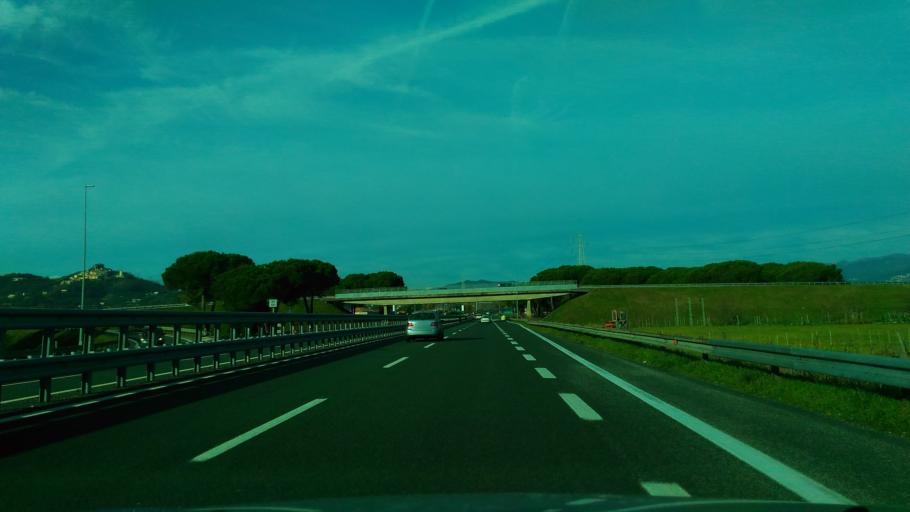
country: IT
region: Liguria
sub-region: Provincia di La Spezia
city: Sarzana
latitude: 44.1001
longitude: 9.9550
